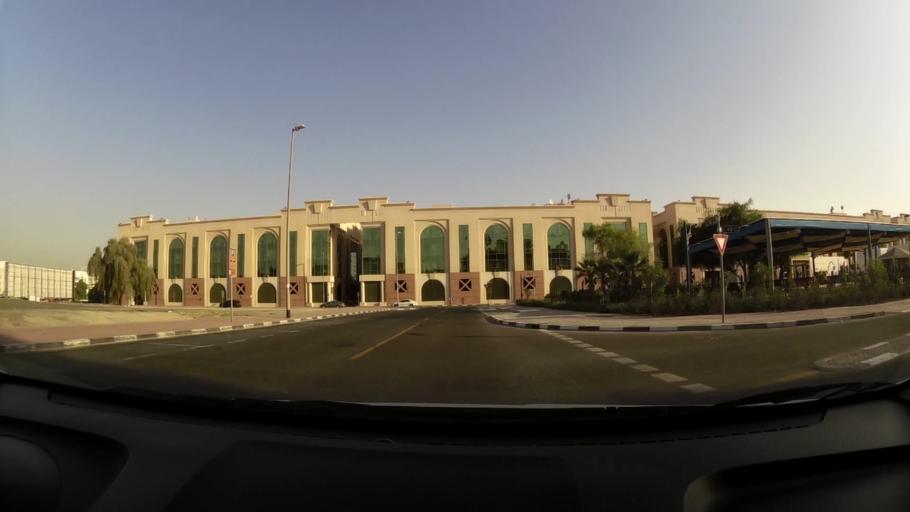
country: AE
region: Ash Shariqah
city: Sharjah
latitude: 25.2465
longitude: 55.3428
